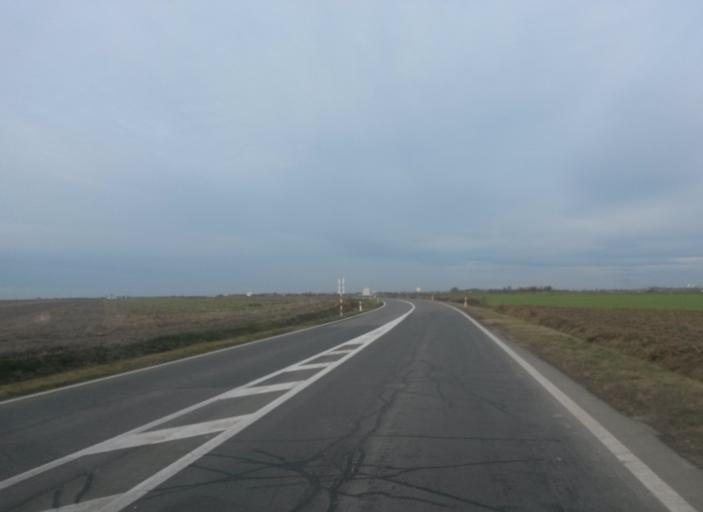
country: HR
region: Osjecko-Baranjska
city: Ovcara
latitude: 45.4972
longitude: 18.5539
